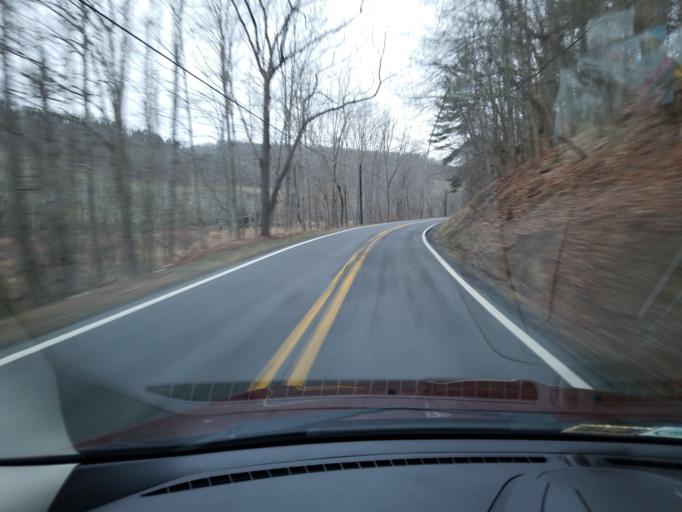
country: US
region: West Virginia
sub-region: Monroe County
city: Union
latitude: 37.5371
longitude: -80.5990
